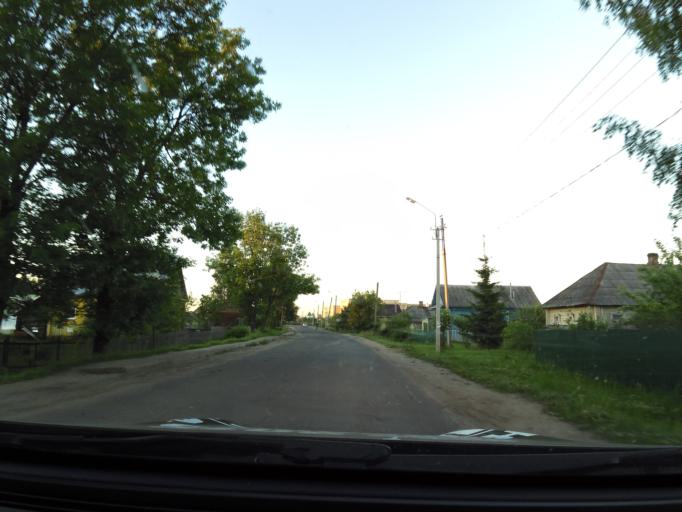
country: RU
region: Jaroslavl
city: Lyubim
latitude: 58.3561
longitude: 40.6916
